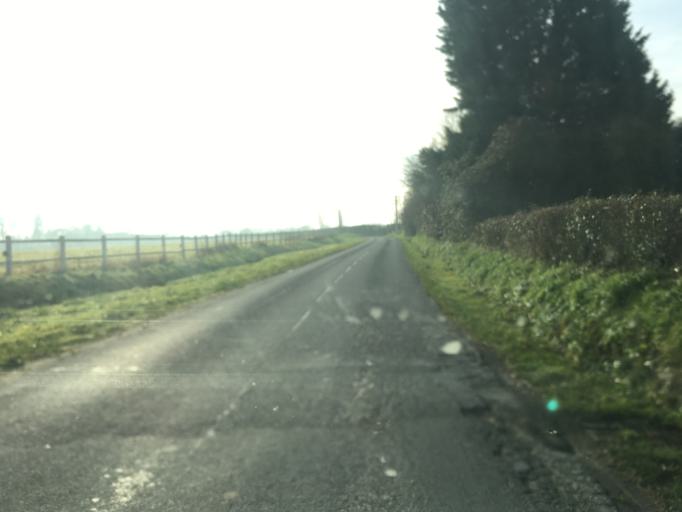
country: FR
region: Lower Normandy
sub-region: Departement du Calvados
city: Dozule
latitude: 49.2107
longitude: -0.0686
